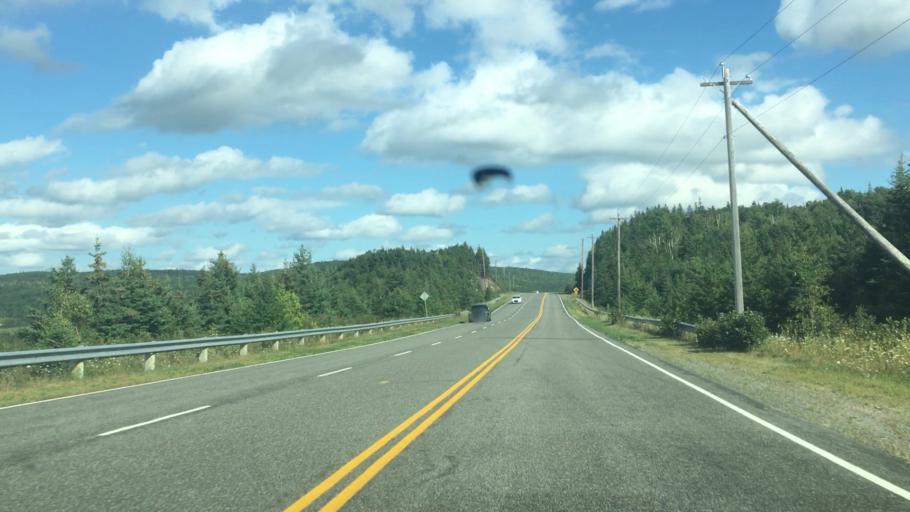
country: CA
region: Nova Scotia
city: Sydney
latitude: 45.8152
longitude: -60.6880
